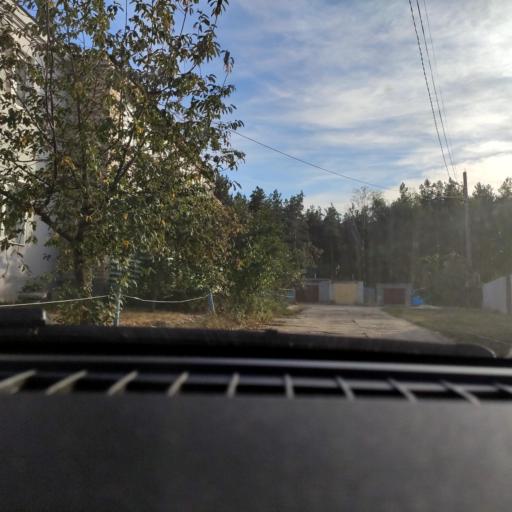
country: RU
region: Voronezj
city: Maslovka
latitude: 51.5805
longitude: 39.2956
